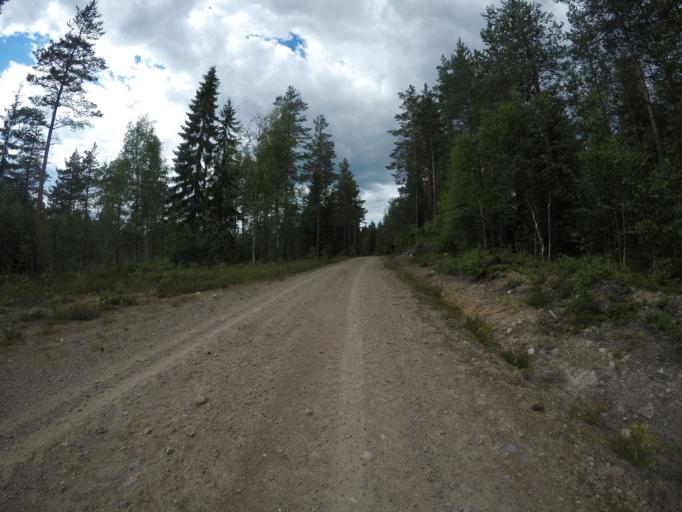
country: SE
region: Vaermland
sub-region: Filipstads Kommun
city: Lesjofors
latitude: 60.0719
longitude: 14.4527
